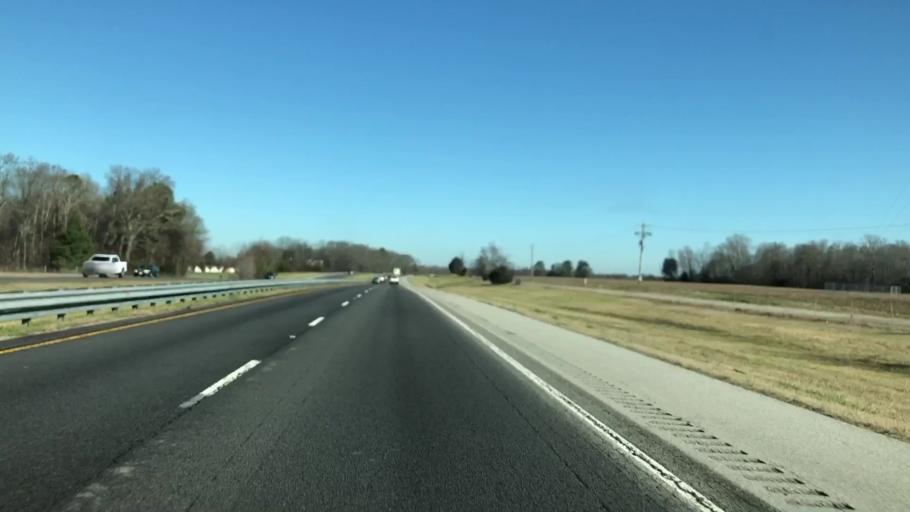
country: US
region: Alabama
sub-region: Limestone County
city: Athens
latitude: 34.8837
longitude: -86.9183
